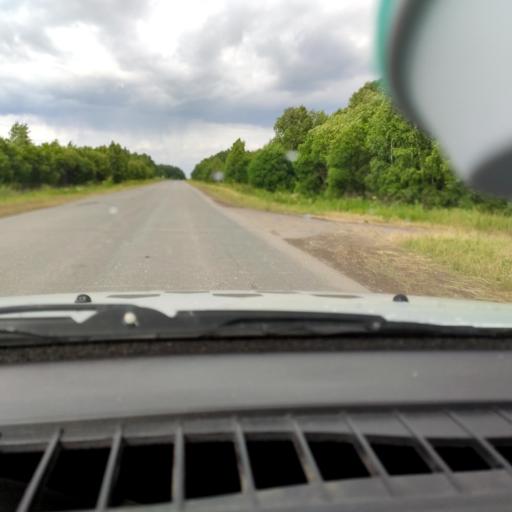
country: RU
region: Perm
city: Orda
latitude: 57.1568
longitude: 56.7986
